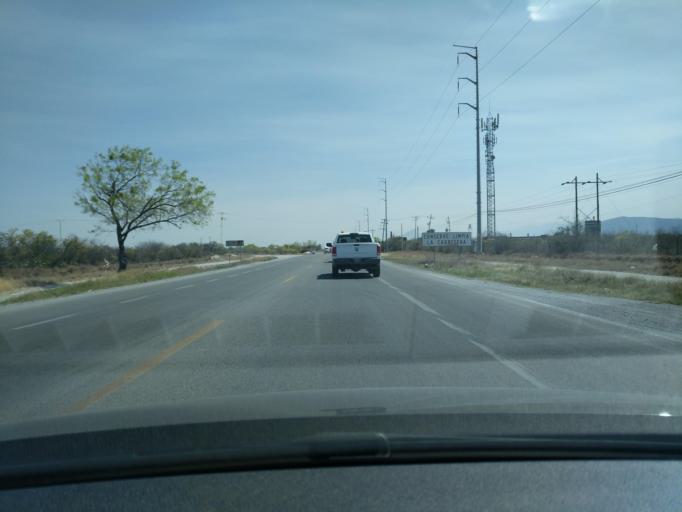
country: MX
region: Nuevo Leon
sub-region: El Carmen
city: Buena Vista
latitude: 25.8966
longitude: -100.3519
